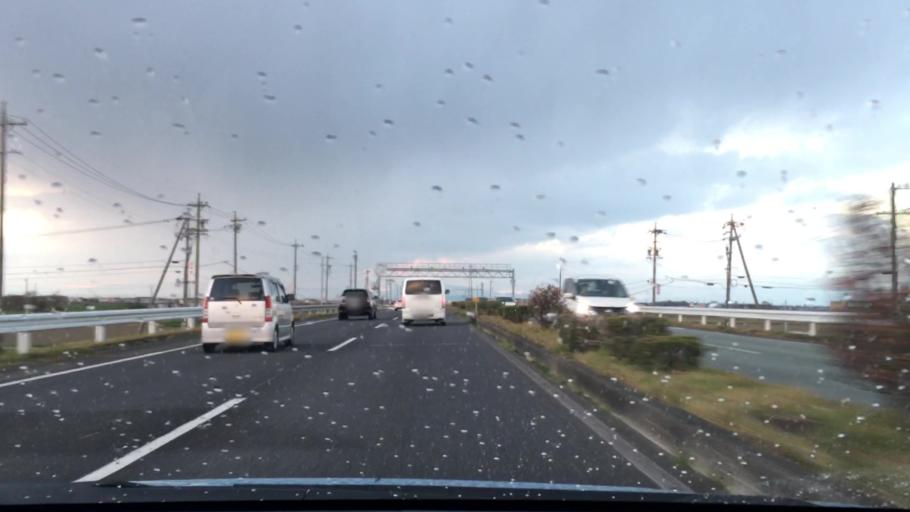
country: JP
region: Mie
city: Ise
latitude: 34.5581
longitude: 136.6478
